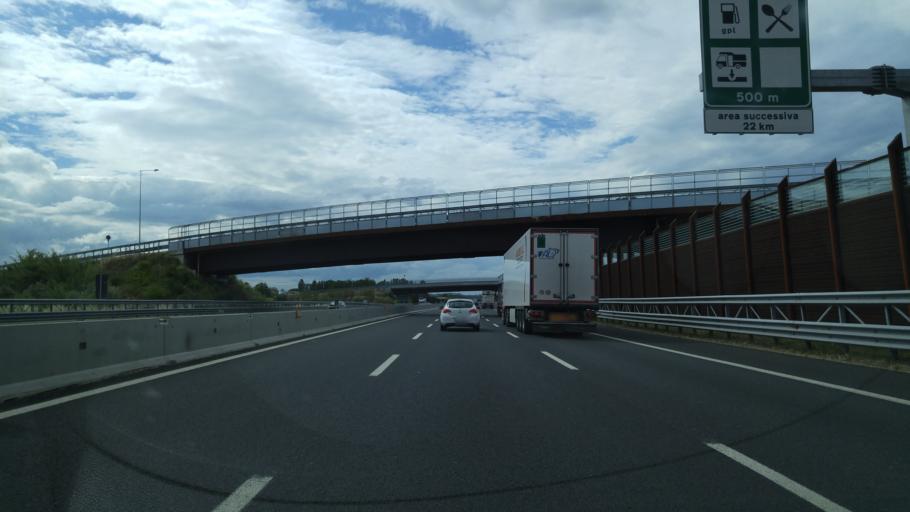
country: IT
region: Emilia-Romagna
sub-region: Provincia di Rimini
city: Riccione
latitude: 43.9912
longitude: 12.6263
